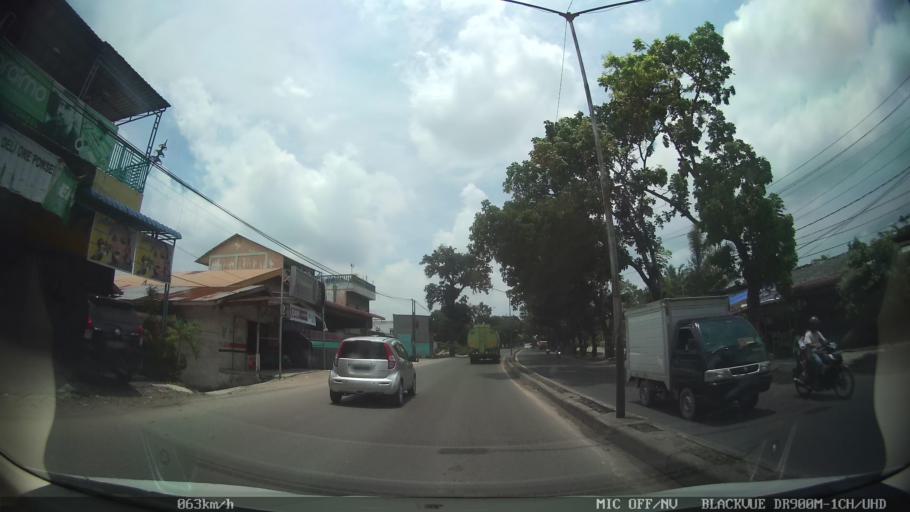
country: ID
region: North Sumatra
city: Labuhan Deli
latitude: 3.7049
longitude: 98.6791
